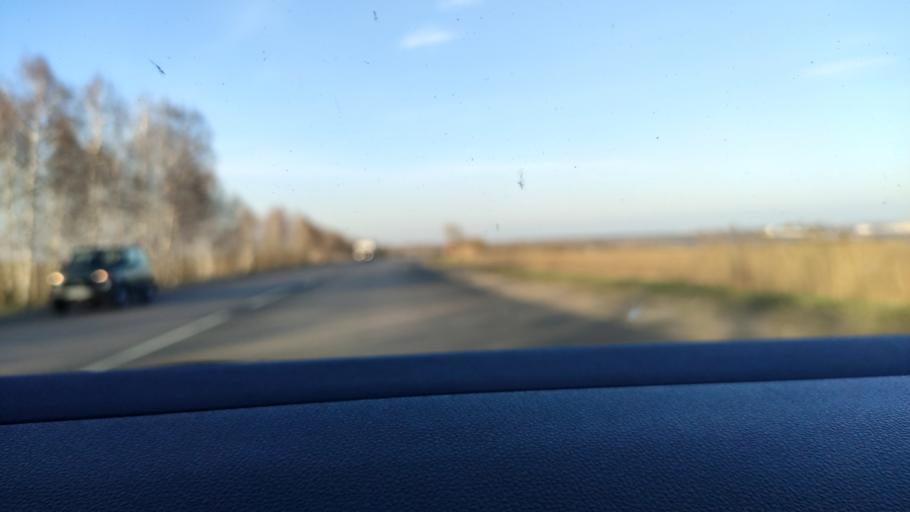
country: RU
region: Voronezj
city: Kolodeznyy
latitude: 51.3272
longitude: 39.1287
